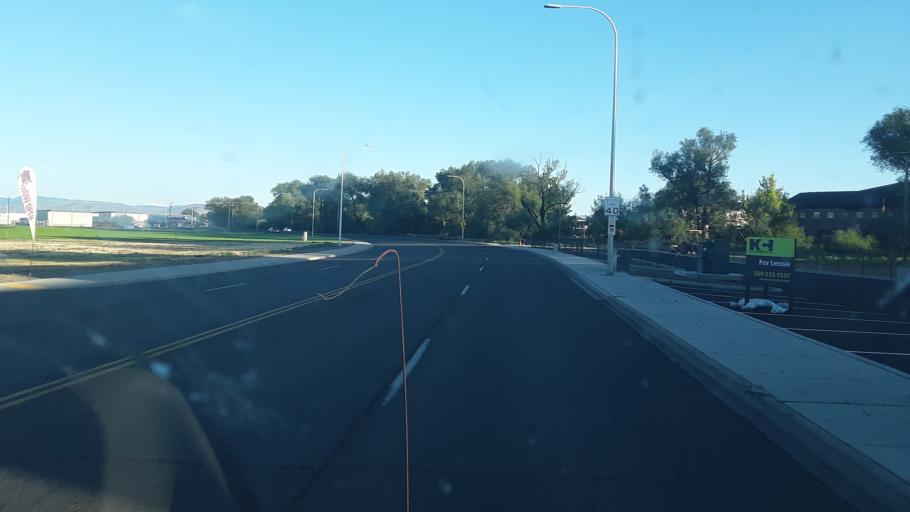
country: US
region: Washington
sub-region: Yakima County
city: Yakima
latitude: 46.5722
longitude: -120.5422
